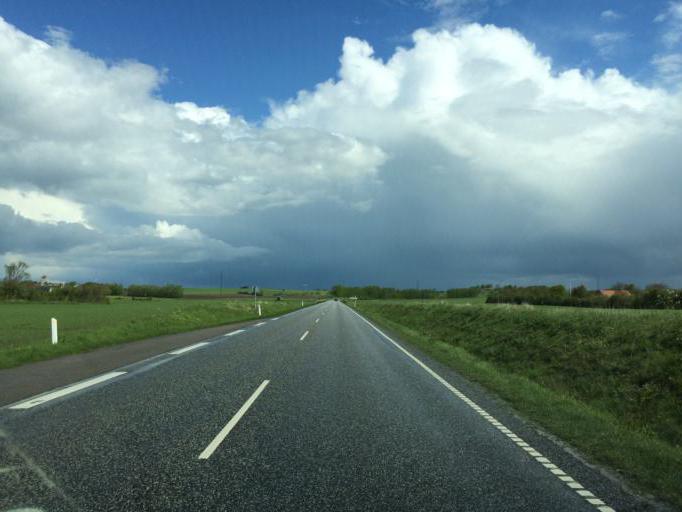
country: DK
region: Central Jutland
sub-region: Holstebro Kommune
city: Vinderup
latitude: 56.4387
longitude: 8.7205
